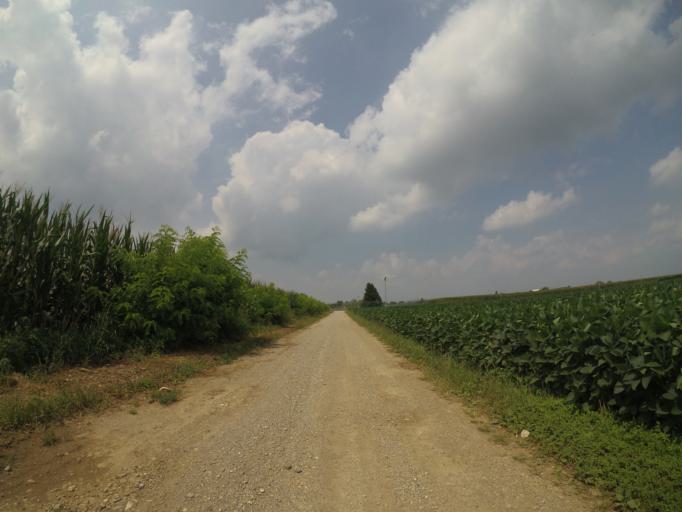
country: IT
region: Friuli Venezia Giulia
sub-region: Provincia di Udine
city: Codroipo
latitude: 45.9838
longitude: 12.9999
